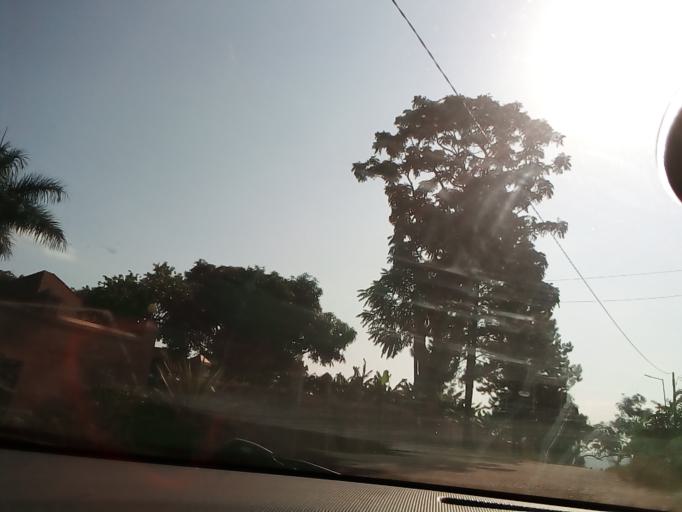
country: UG
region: Central Region
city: Masaka
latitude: -0.3332
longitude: 31.7362
